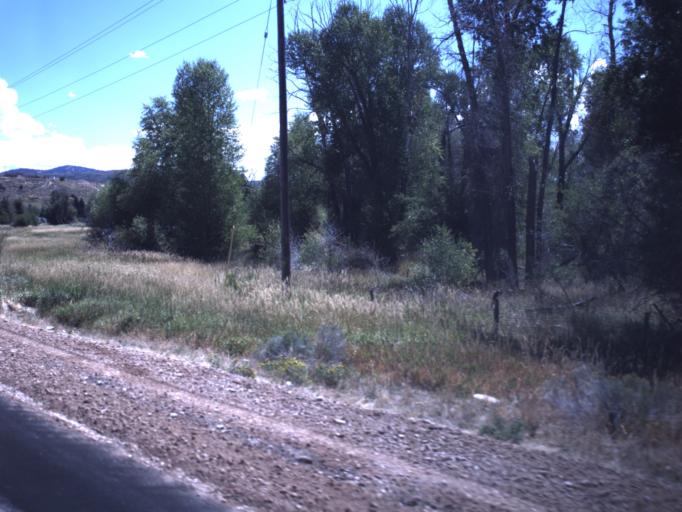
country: US
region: Utah
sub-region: Summit County
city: Francis
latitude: 40.6115
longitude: -111.3017
